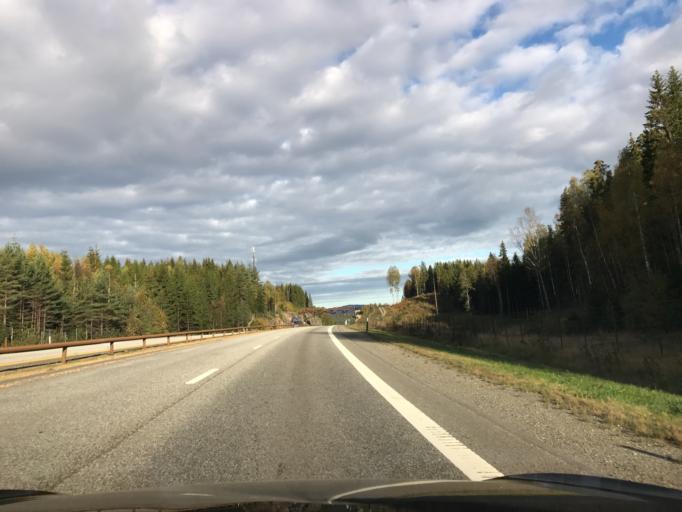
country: NO
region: Akershus
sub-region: Eidsvoll
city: Raholt
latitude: 60.2720
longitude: 11.1541
